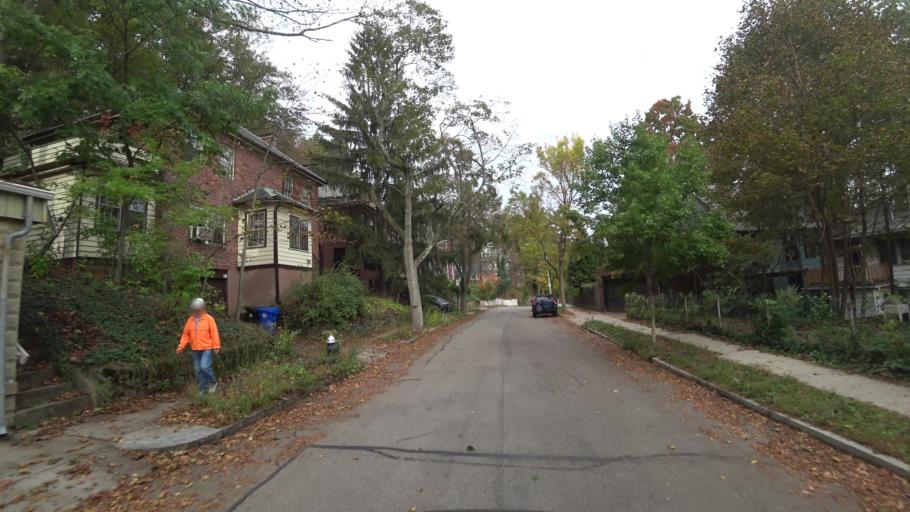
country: US
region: Massachusetts
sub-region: Norfolk County
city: Brookline
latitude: 42.3430
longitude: -71.1283
